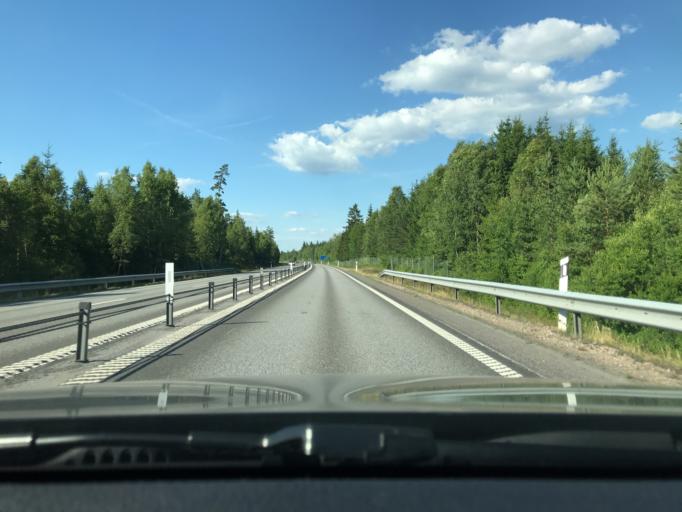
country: SE
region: Kronoberg
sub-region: Almhults Kommun
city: AElmhult
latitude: 56.4671
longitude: 14.1031
